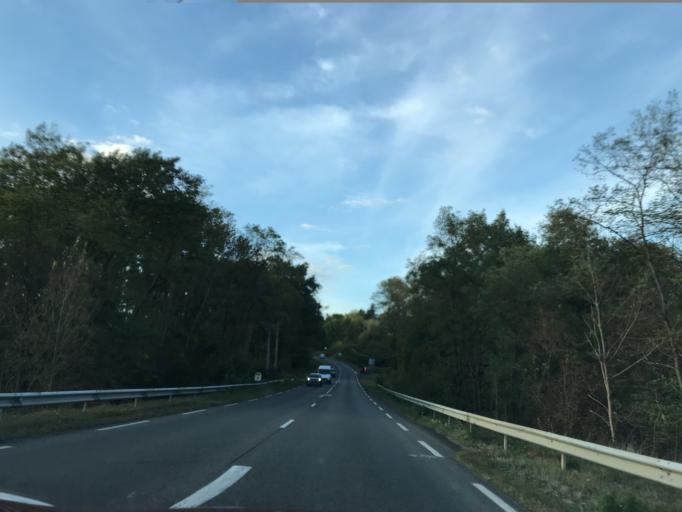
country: FR
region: Auvergne
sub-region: Departement de l'Allier
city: Saint-Yorre
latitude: 46.0793
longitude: 3.4627
